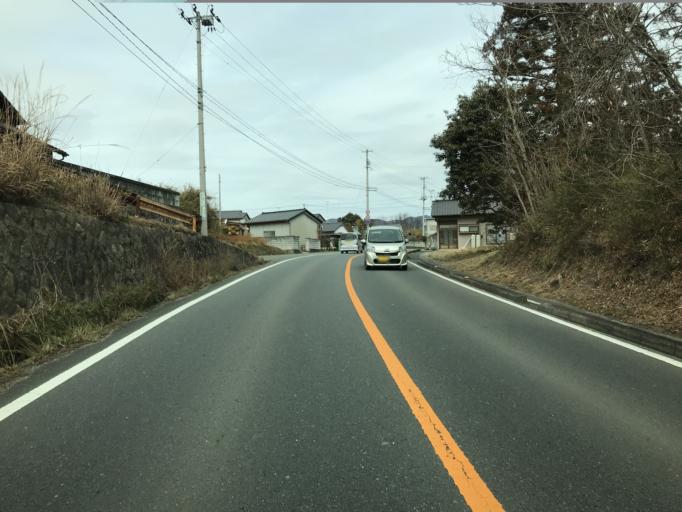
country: JP
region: Fukushima
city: Iwaki
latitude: 37.0971
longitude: 140.8737
